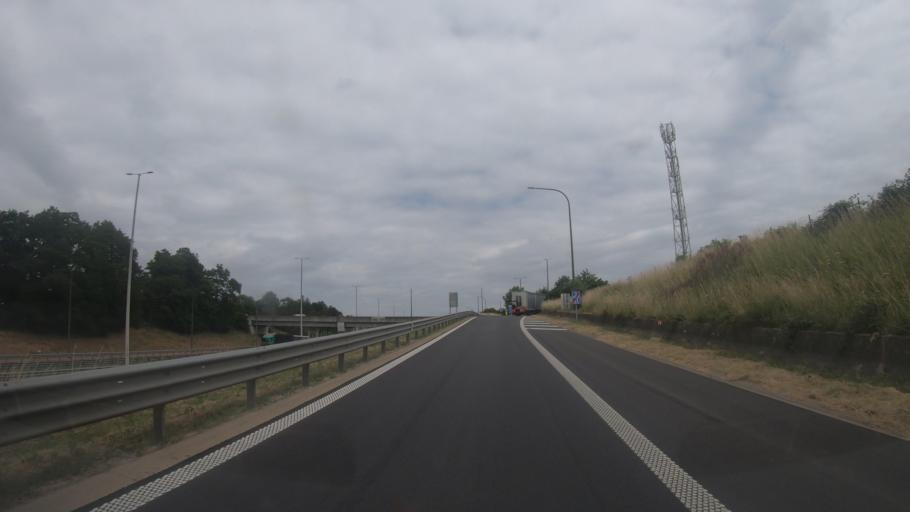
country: BE
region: Wallonia
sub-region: Province de Liege
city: Dison
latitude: 50.6440
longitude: 5.8908
